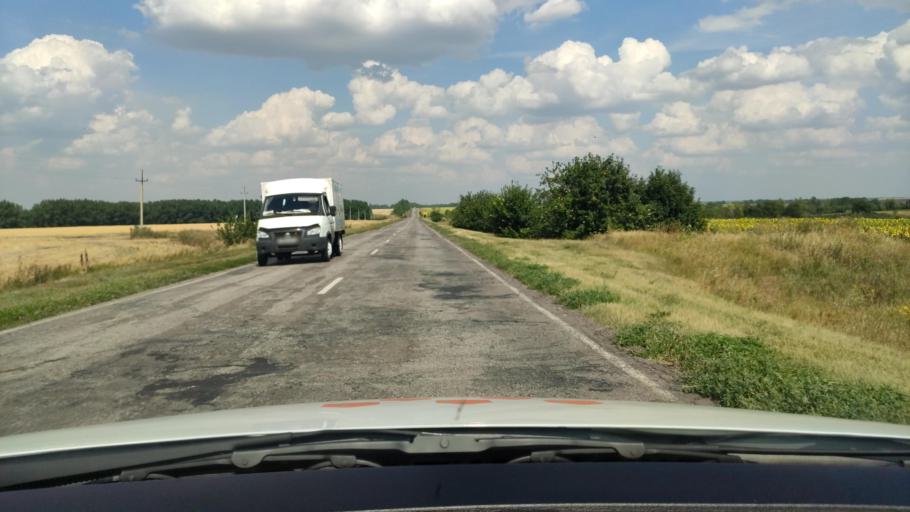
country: RU
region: Voronezj
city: Pereleshinskiy
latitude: 51.7420
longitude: 40.3994
